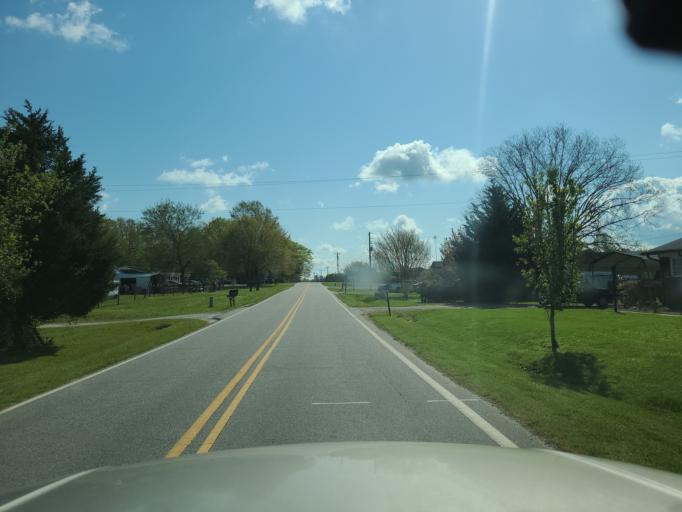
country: US
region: North Carolina
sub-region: Rutherford County
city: Spindale
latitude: 35.2966
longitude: -81.9203
